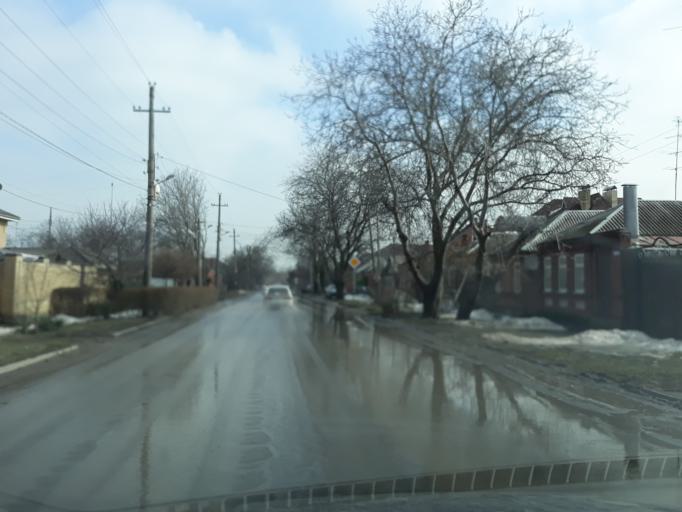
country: RU
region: Rostov
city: Taganrog
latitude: 47.2144
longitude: 38.9026
